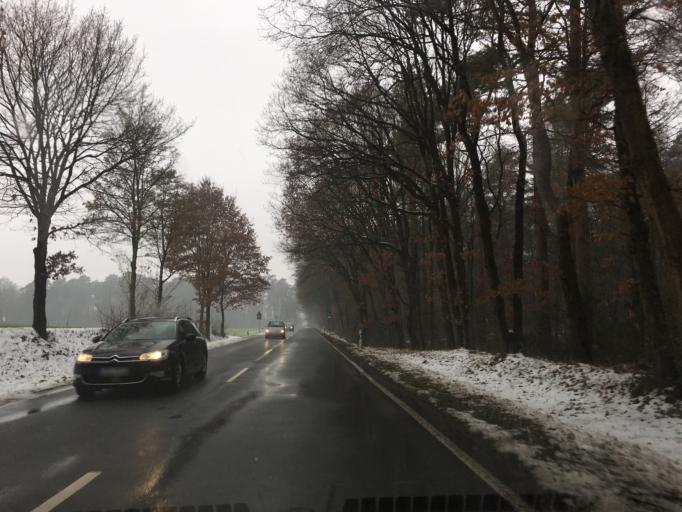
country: DE
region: North Rhine-Westphalia
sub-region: Regierungsbezirk Munster
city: Klein Reken
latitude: 51.7824
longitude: 7.0894
